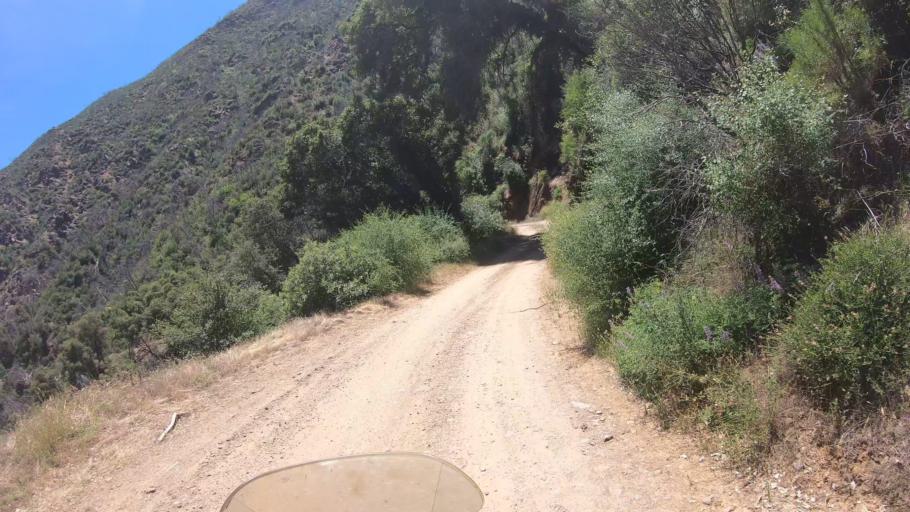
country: US
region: California
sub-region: Tuolumne County
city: Tuolumne City
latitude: 37.8343
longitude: -120.0692
